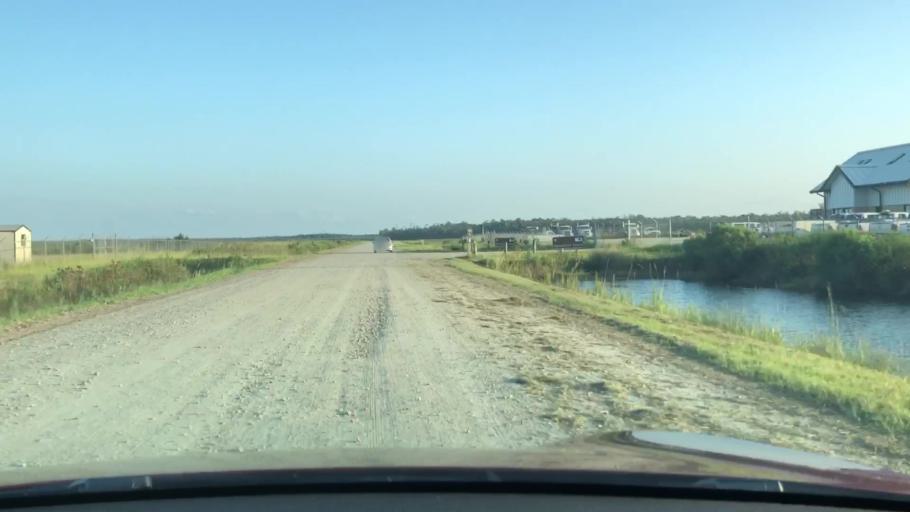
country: US
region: North Carolina
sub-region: Dare County
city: Manteo
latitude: 35.8551
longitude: -75.8625
